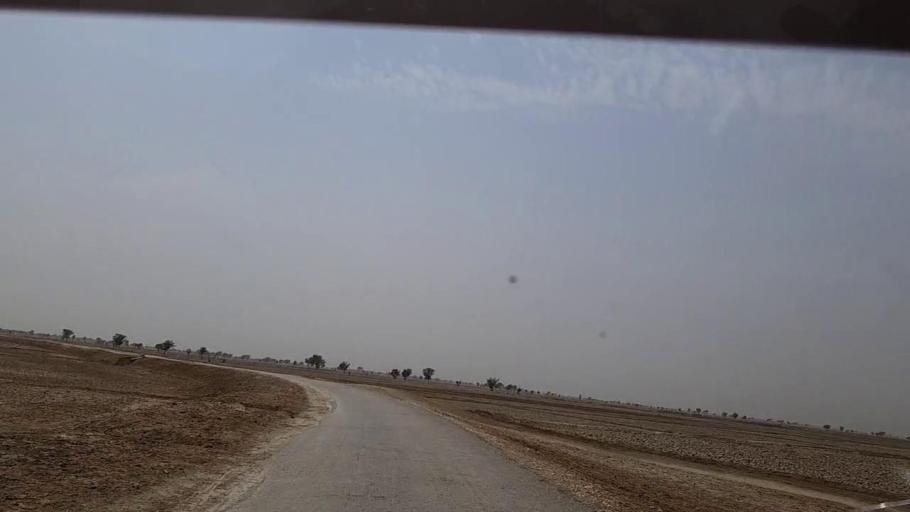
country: PK
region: Sindh
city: Khairpur Nathan Shah
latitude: 27.0189
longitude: 67.6212
